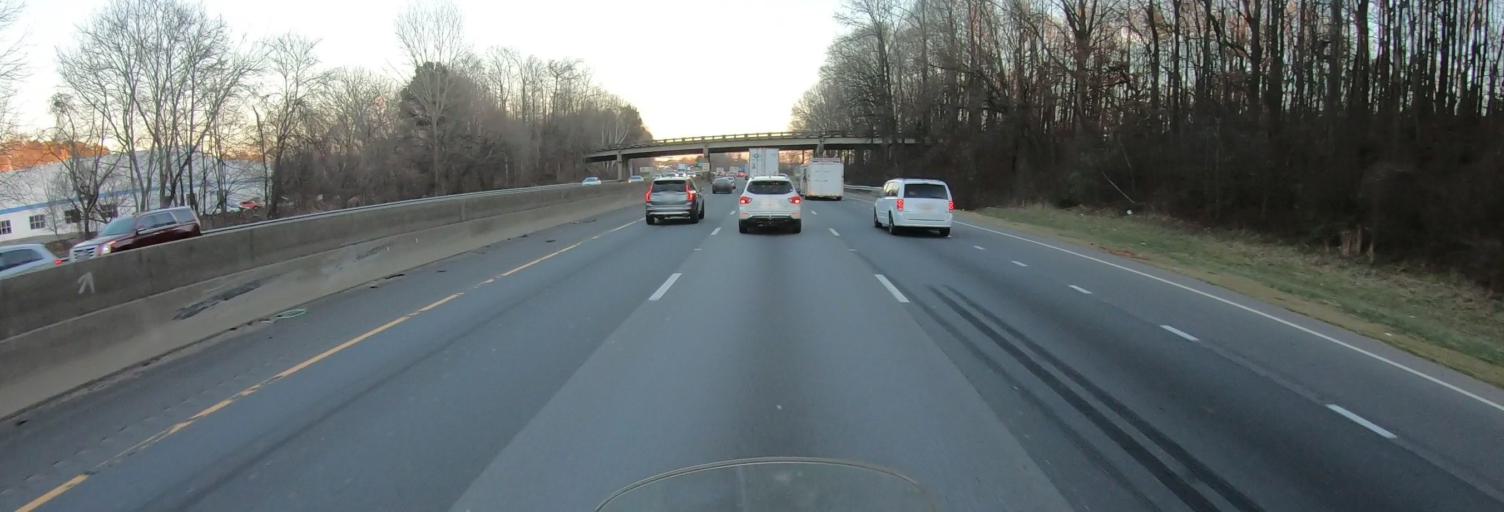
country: US
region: North Carolina
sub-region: Gaston County
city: Ranlo
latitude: 35.2684
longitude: -81.1433
